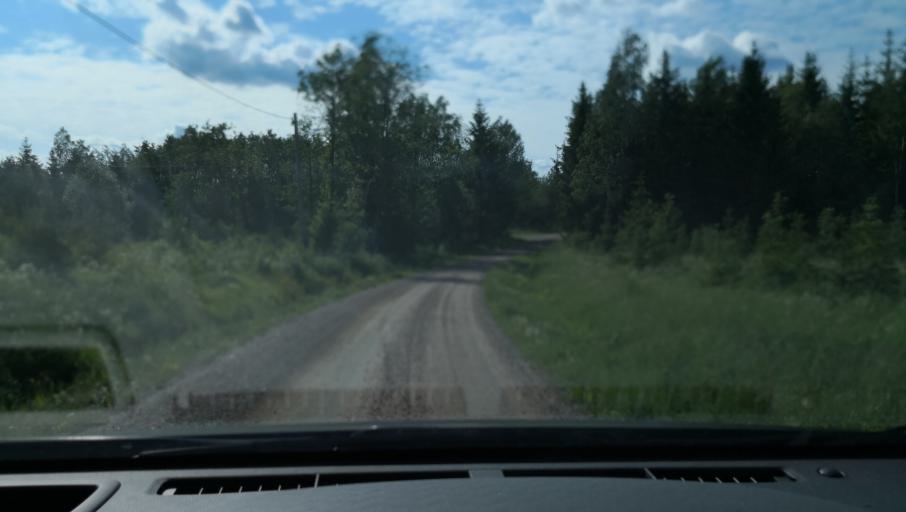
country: SE
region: Uppsala
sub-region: Enkopings Kommun
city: Orsundsbro
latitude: 59.8337
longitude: 17.2391
